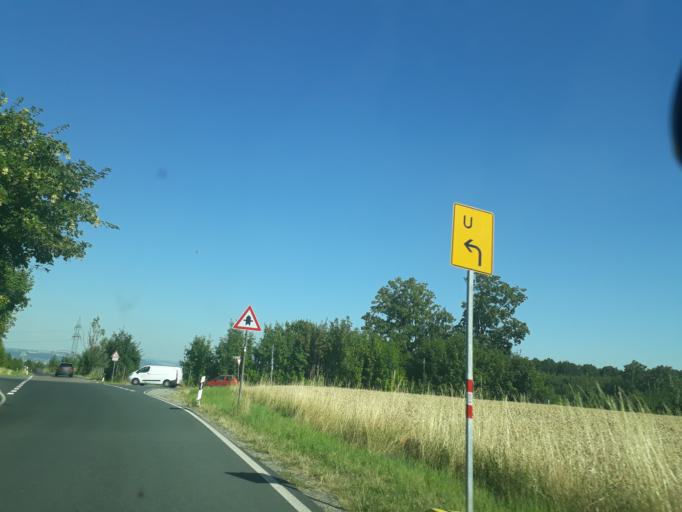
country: DE
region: Saxony
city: Freital
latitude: 51.0233
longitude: 13.6663
